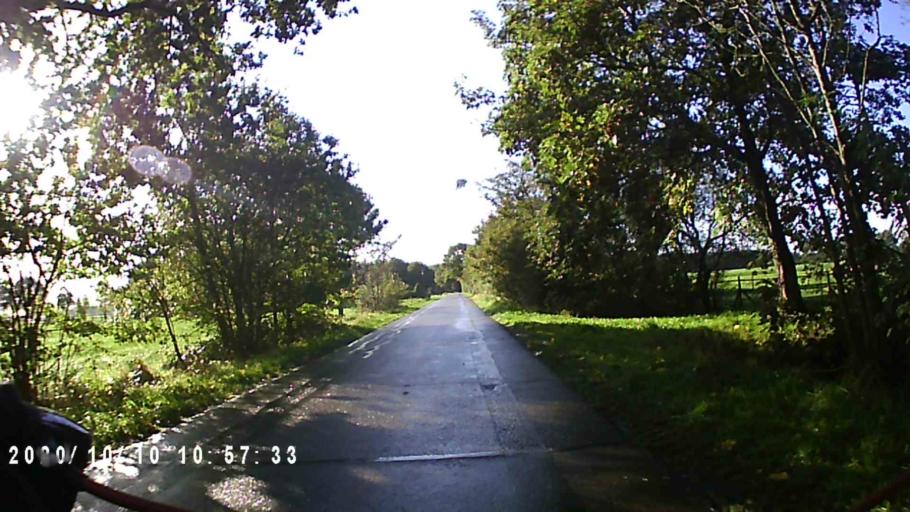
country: NL
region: Friesland
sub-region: Gemeente Achtkarspelen
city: Surhuisterveen
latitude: 53.1479
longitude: 6.2064
